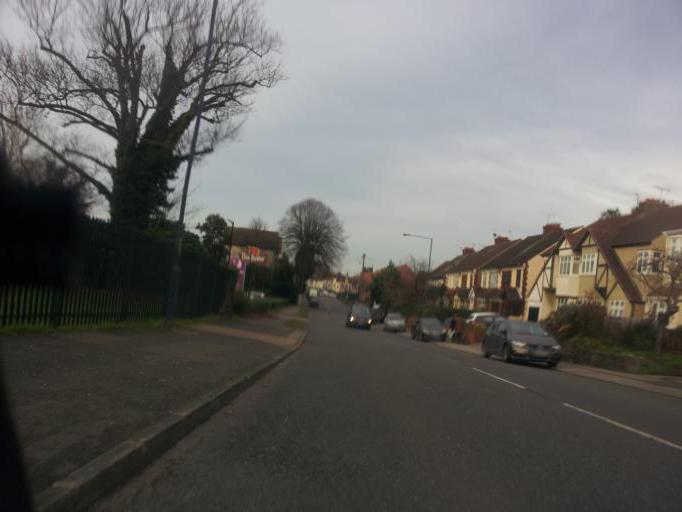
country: GB
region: England
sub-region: Kent
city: Gravesend
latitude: 51.4312
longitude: 0.3645
